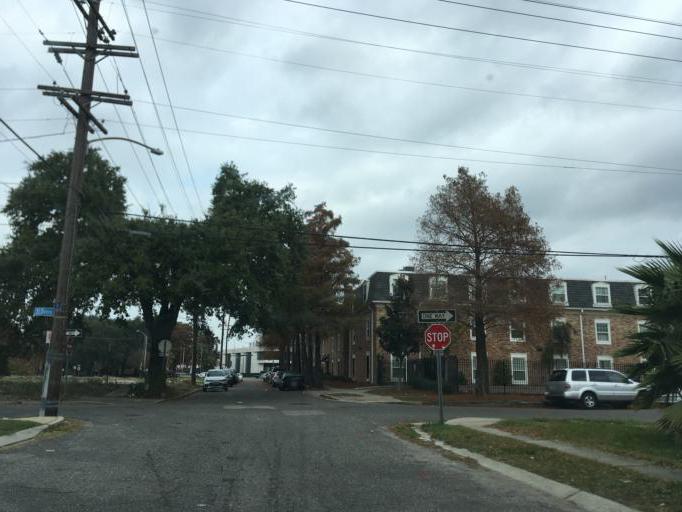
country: US
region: Louisiana
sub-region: Orleans Parish
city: New Orleans
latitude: 29.9955
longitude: -90.0615
